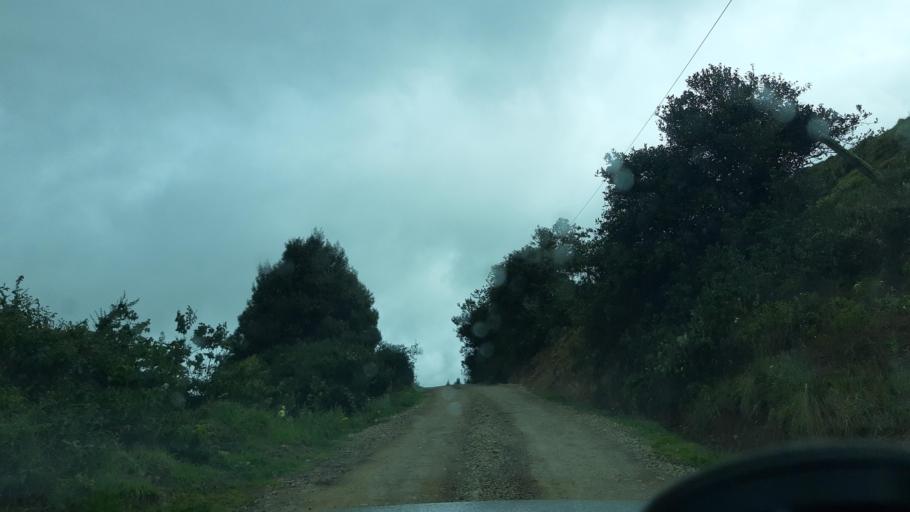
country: CO
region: Boyaca
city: Cucaita
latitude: 5.5074
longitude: -73.4340
